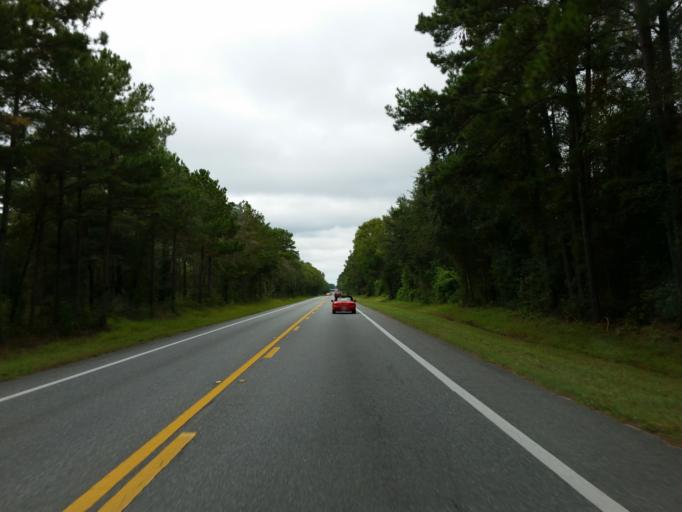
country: US
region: Florida
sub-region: Columbia County
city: Five Points
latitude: 30.2300
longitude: -82.6639
